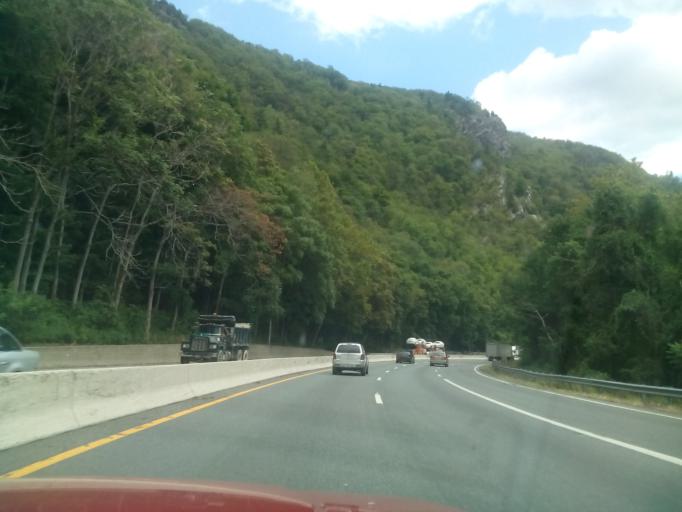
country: US
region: Pennsylvania
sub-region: Monroe County
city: East Stroudsburg
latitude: 40.9714
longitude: -75.1223
